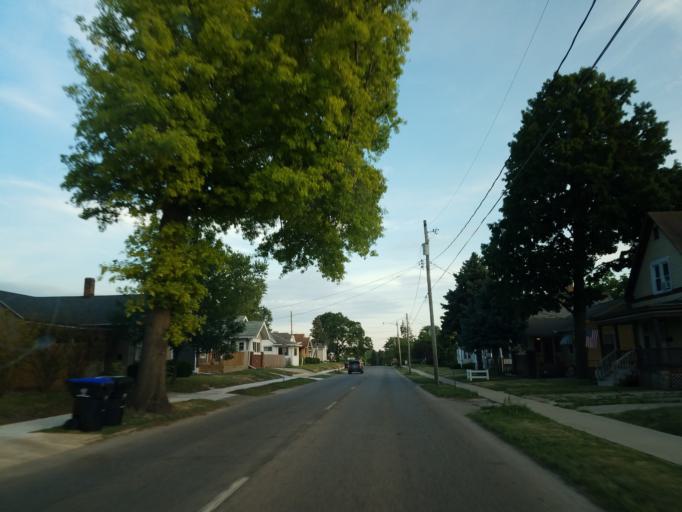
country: US
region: Illinois
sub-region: McLean County
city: Bloomington
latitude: 40.4648
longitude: -88.9940
